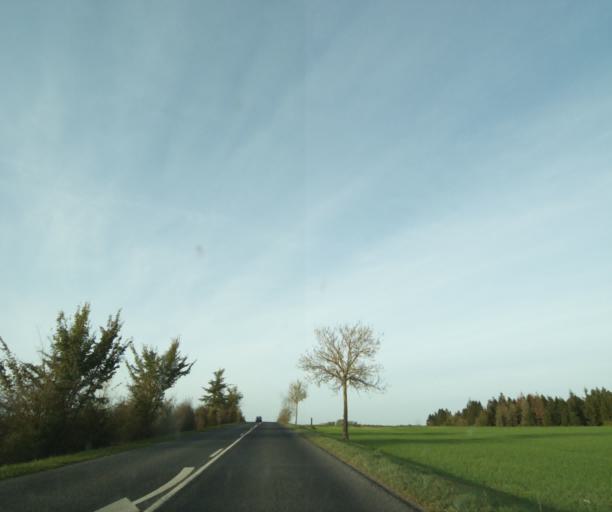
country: FR
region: Lorraine
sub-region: Departement de la Meuse
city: Etain
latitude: 49.2496
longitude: 5.6670
